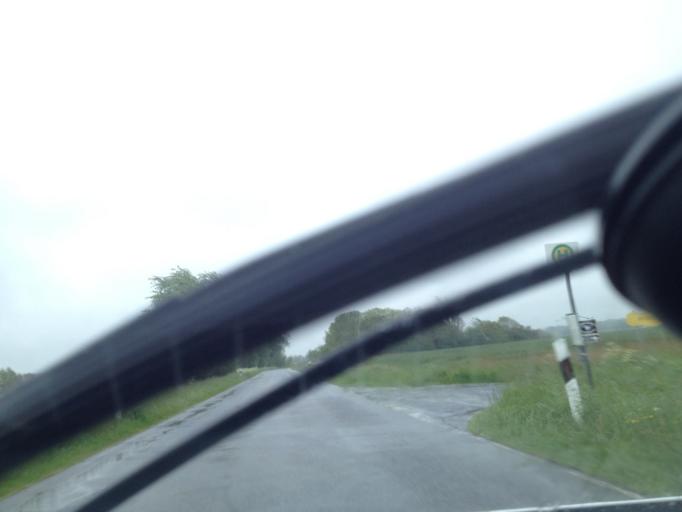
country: DE
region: Schleswig-Holstein
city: Neukirchen
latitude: 54.8801
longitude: 8.7270
